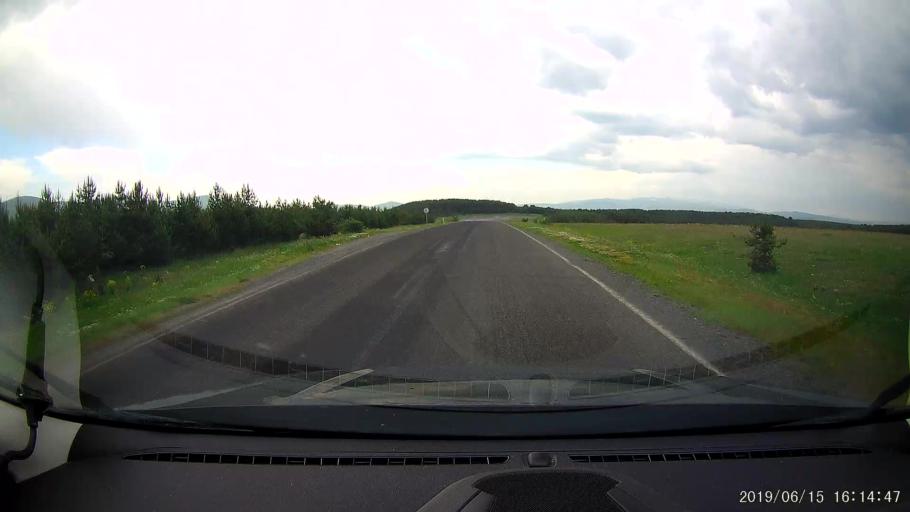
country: TR
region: Ardahan
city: Hanak
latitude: 41.2754
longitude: 42.8487
